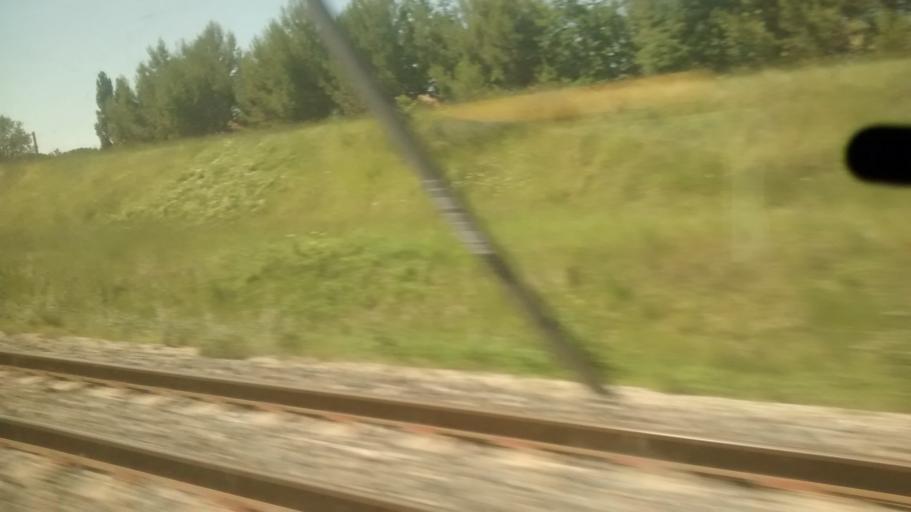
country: FR
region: Rhone-Alpes
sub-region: Departement de la Drome
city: Montboucher-sur-Jabron
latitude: 44.5524
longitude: 4.8297
